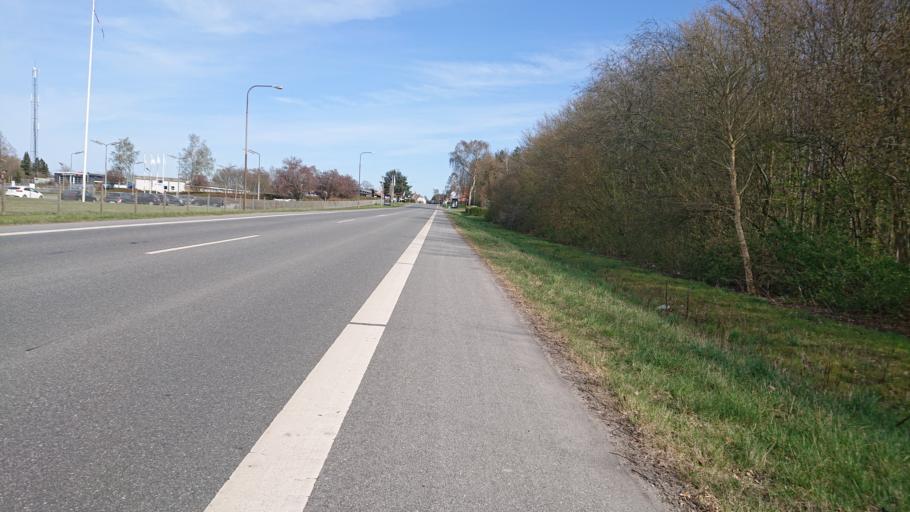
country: DK
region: South Denmark
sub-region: Nyborg Kommune
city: Nyborg
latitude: 55.3093
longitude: 10.7594
